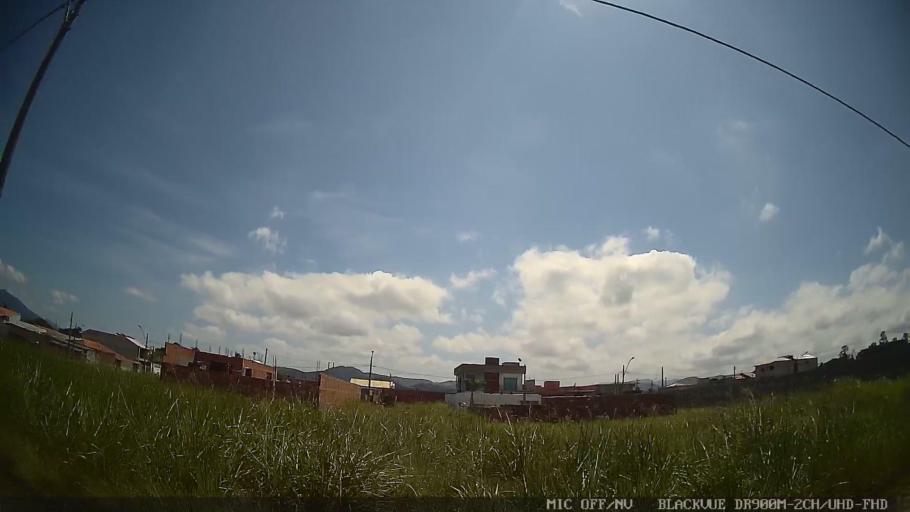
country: BR
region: Sao Paulo
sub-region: Peruibe
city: Peruibe
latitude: -24.3014
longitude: -46.9988
